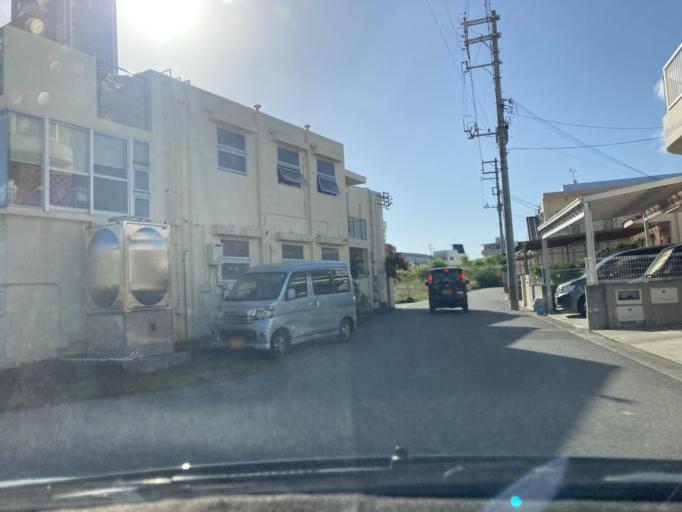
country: JP
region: Okinawa
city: Ginowan
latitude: 26.2378
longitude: 127.7264
